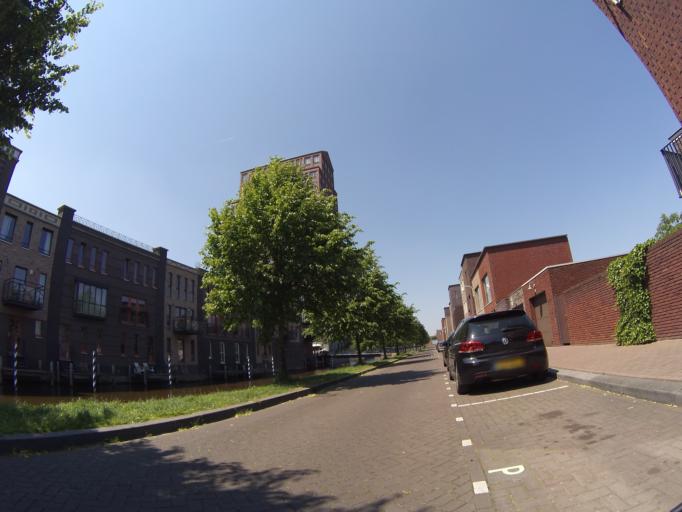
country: NL
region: Gelderland
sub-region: Gemeente Nijkerk
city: Nijkerk
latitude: 52.1975
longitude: 5.4363
